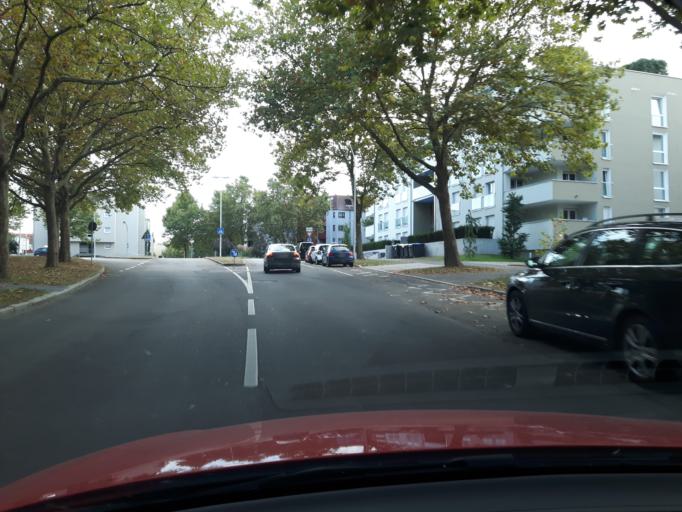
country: DE
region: Baden-Wuerttemberg
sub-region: Regierungsbezirk Stuttgart
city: Flein
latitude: 49.1227
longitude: 9.2067
